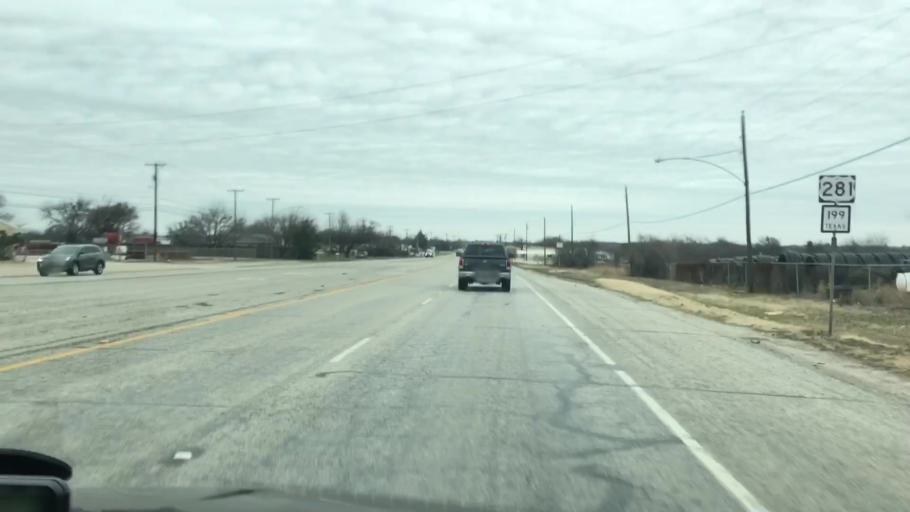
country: US
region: Texas
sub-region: Jack County
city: Jacksboro
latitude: 33.2040
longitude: -98.1520
